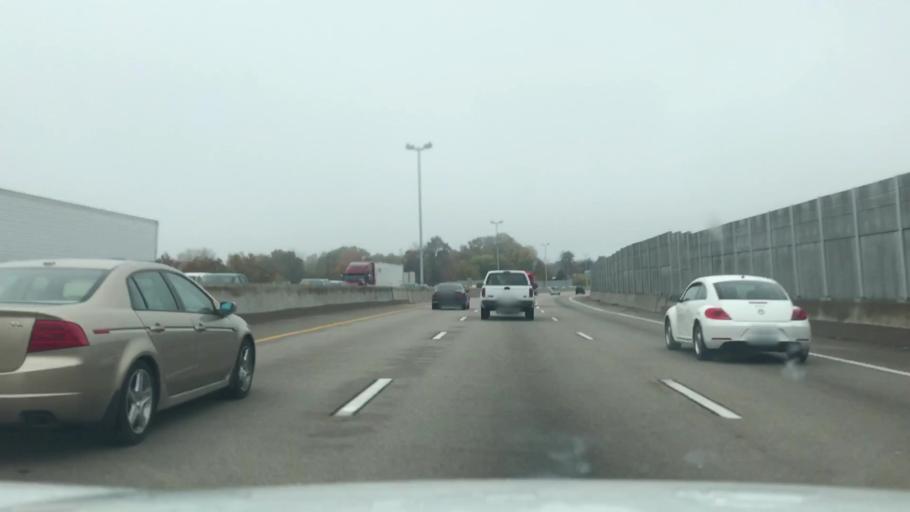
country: US
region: Missouri
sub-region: Saint Louis County
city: Richmond Heights
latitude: 38.6302
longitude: -90.3062
